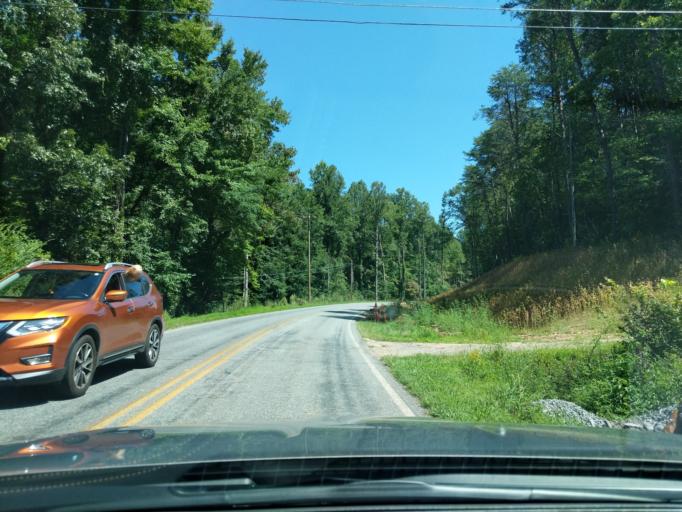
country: US
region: Georgia
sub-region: Towns County
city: Hiawassee
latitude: 35.0119
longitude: -83.7413
